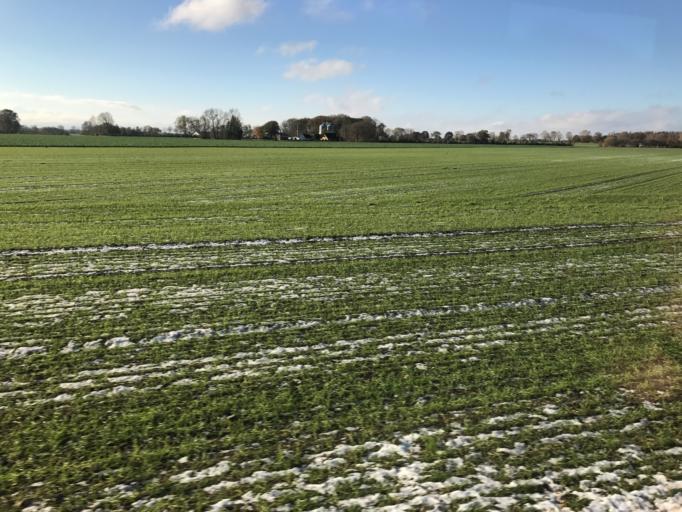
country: DK
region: Zealand
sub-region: Stevns Kommune
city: Store Heddinge
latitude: 55.3434
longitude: 12.3305
